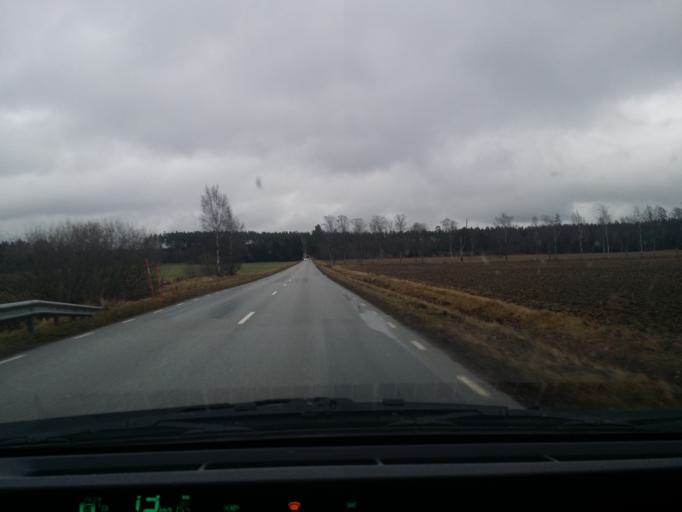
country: SE
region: Vaestmanland
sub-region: Sala Kommun
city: Sala
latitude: 59.8095
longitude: 16.5316
